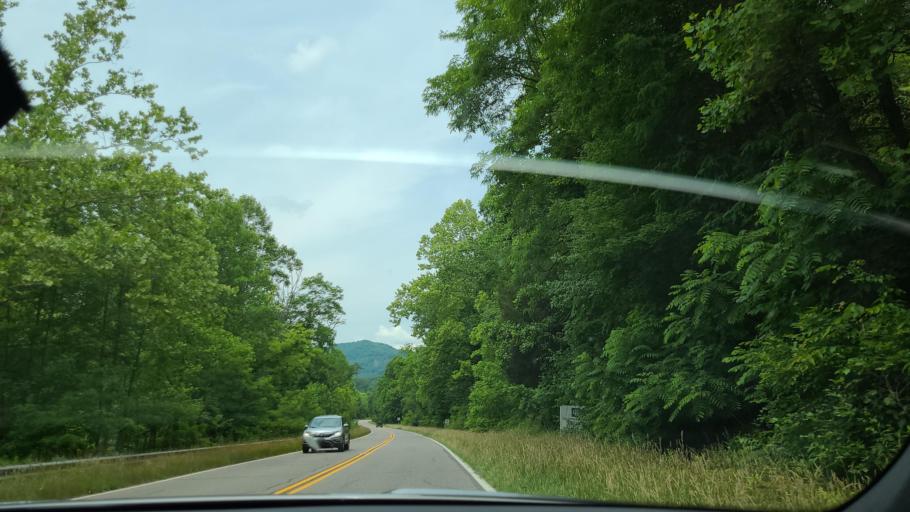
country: US
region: North Carolina
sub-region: Macon County
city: Franklin
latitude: 35.1426
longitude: -83.2913
